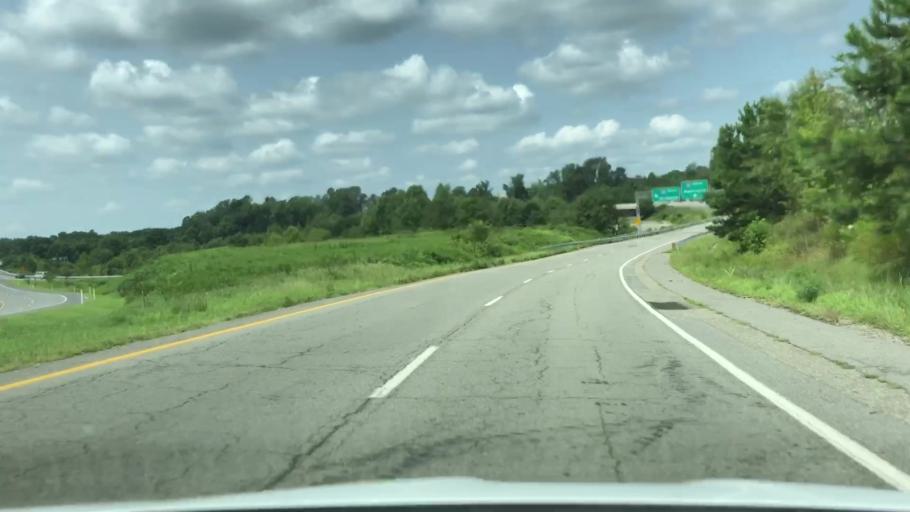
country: US
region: Virginia
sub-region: Henrico County
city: Glen Allen
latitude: 37.6888
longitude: -77.4467
